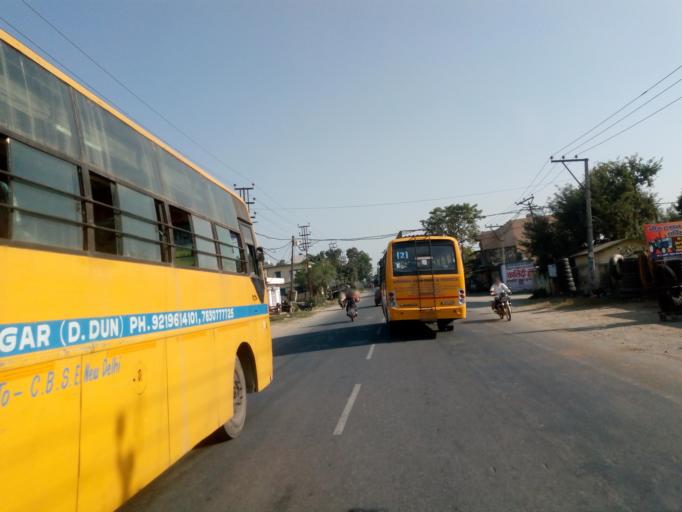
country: IN
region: Uttarakhand
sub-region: Dehradun
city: Harbatpur
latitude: 30.3980
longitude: 77.8001
